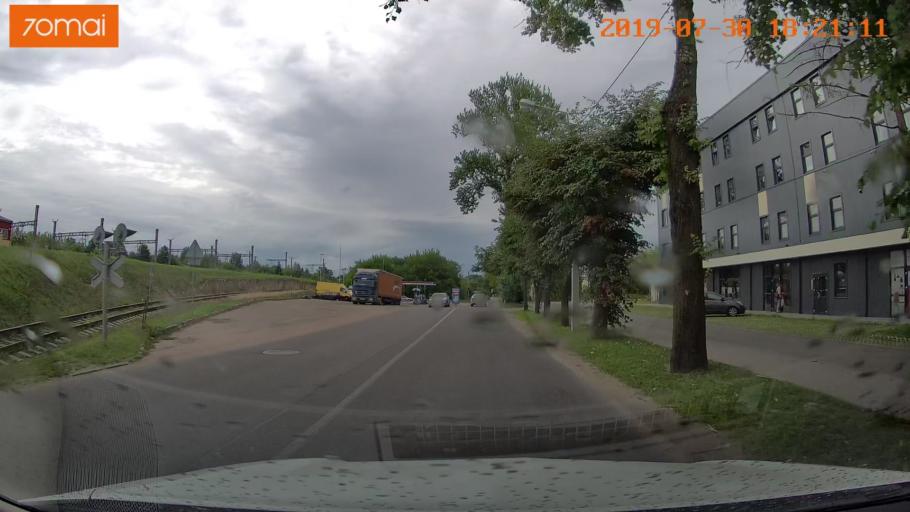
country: LT
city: Skaidiskes
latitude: 54.6957
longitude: 25.4302
